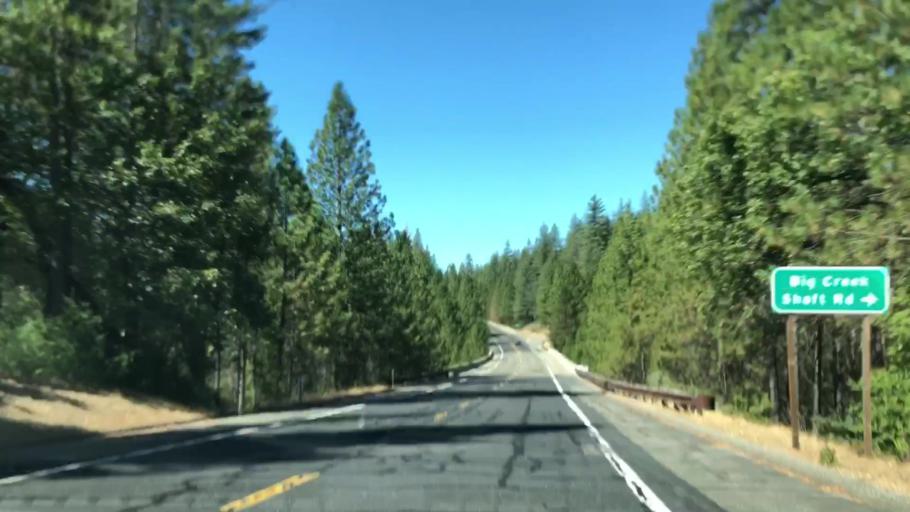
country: US
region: California
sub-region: Tuolumne County
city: Tuolumne City
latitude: 37.8210
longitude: -120.1465
